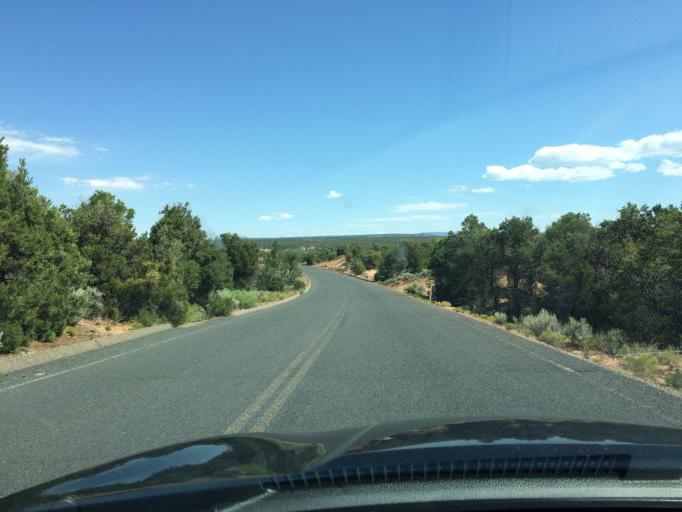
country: US
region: Arizona
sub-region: Apache County
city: Chinle
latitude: 36.0992
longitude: -109.3723
